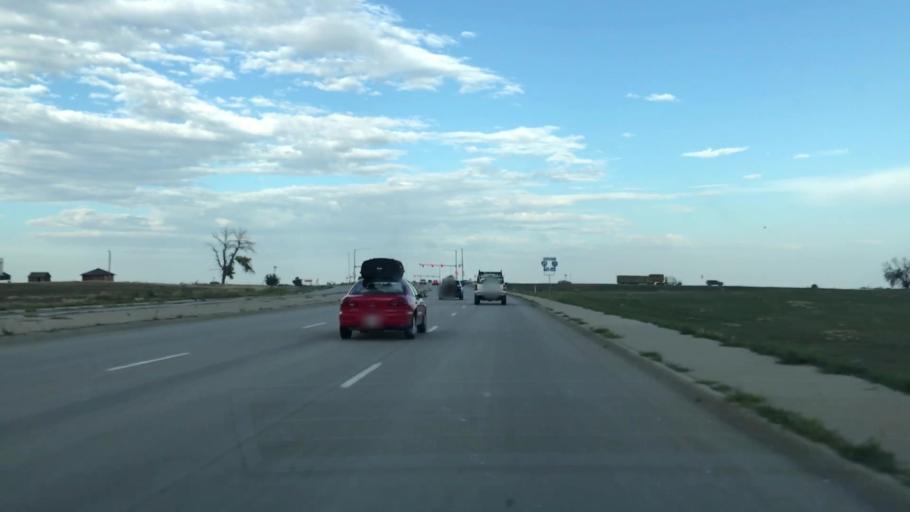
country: US
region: Colorado
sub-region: Weld County
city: Mead
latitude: 40.2041
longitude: -104.9847
